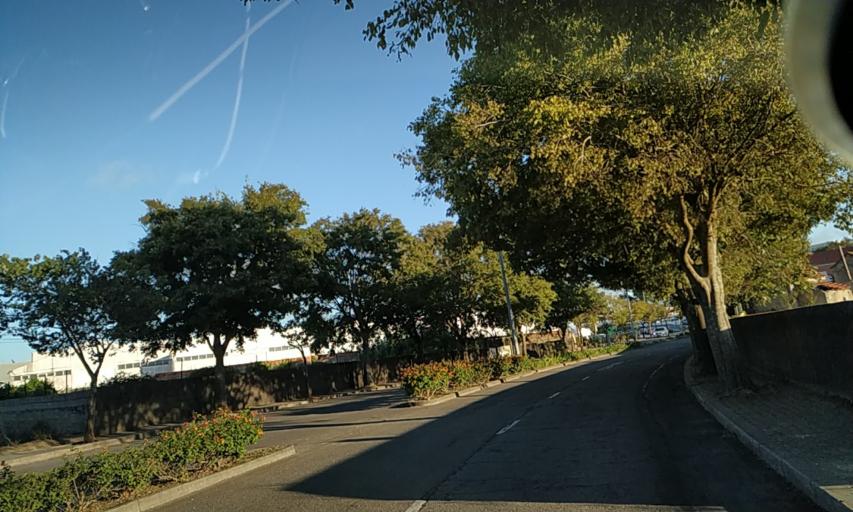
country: PT
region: Aveiro
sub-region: Aveiro
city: Aradas
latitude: 40.6324
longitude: -8.6435
